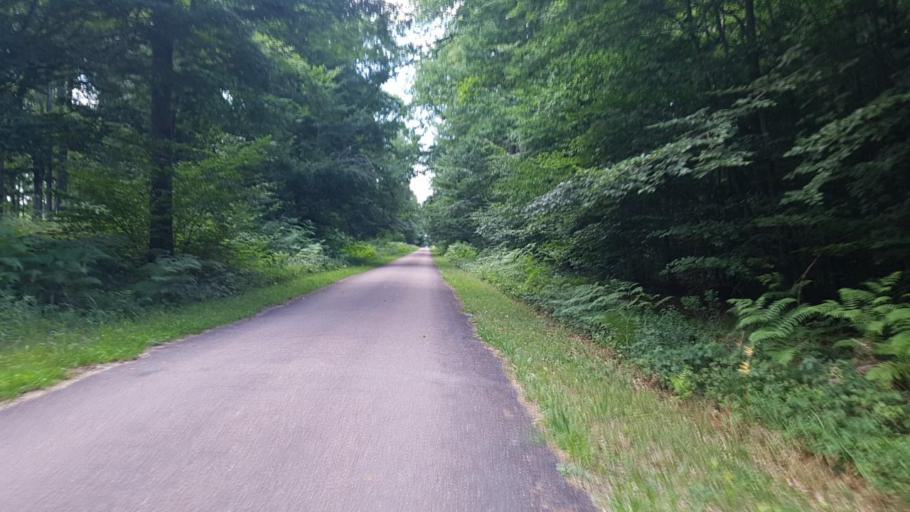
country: FR
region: Picardie
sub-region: Departement de l'Oise
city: Chamant
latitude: 49.1586
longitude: 2.6365
